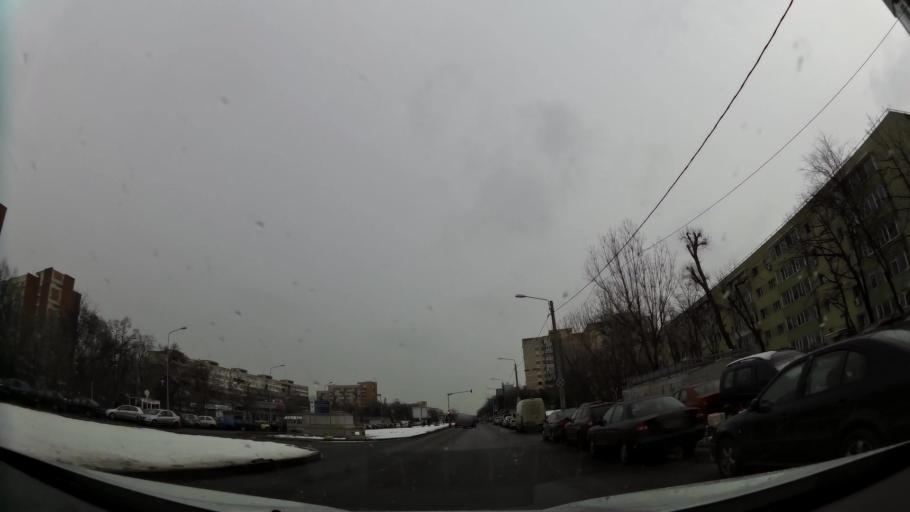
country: RO
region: Ilfov
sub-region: Comuna Chiajna
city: Rosu
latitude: 44.4234
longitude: 26.0390
